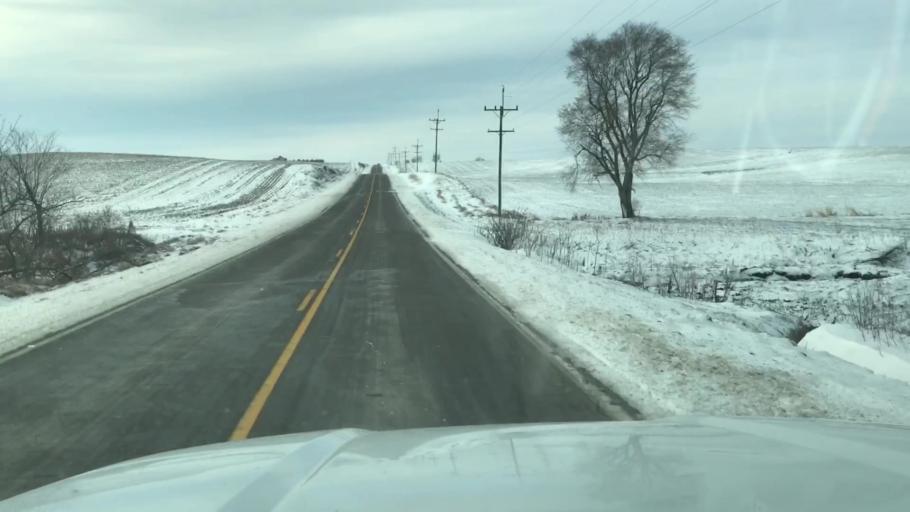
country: US
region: Missouri
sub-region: Holt County
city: Mound City
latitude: 40.1108
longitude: -95.1449
